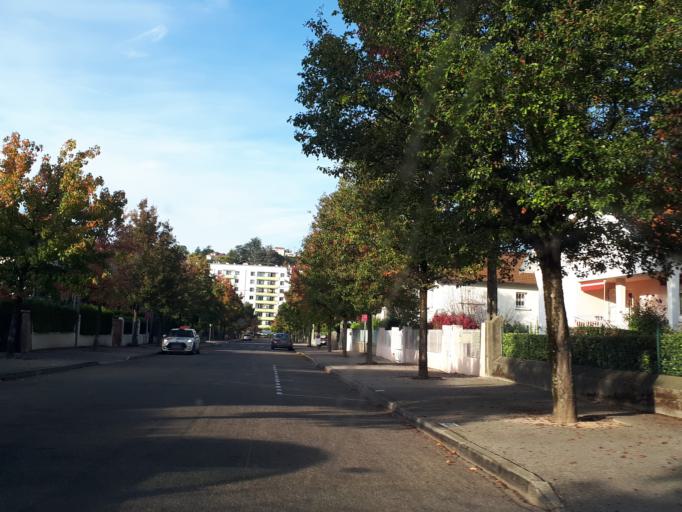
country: FR
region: Rhone-Alpes
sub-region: Departement de l'Isere
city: Bourgoin
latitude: 45.5906
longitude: 5.2868
